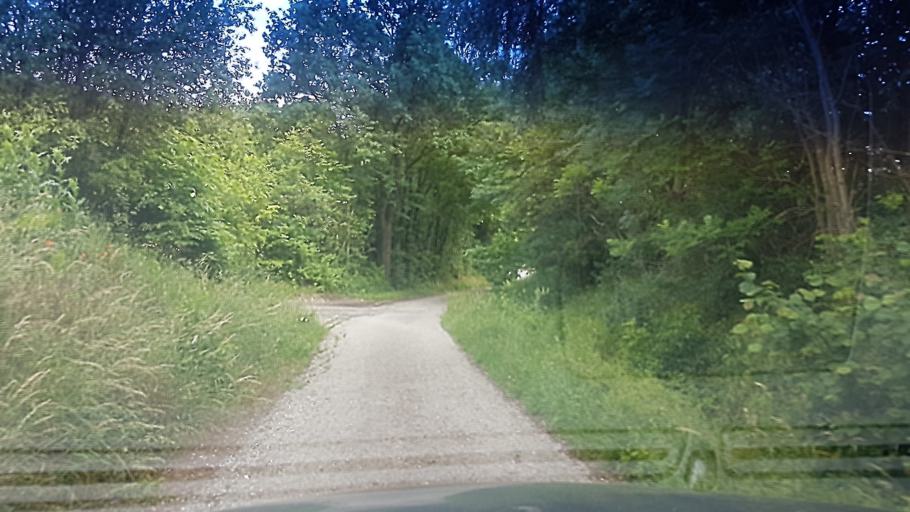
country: DE
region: Bavaria
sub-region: Upper Franconia
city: Buttenheim
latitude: 49.8294
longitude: 11.0544
